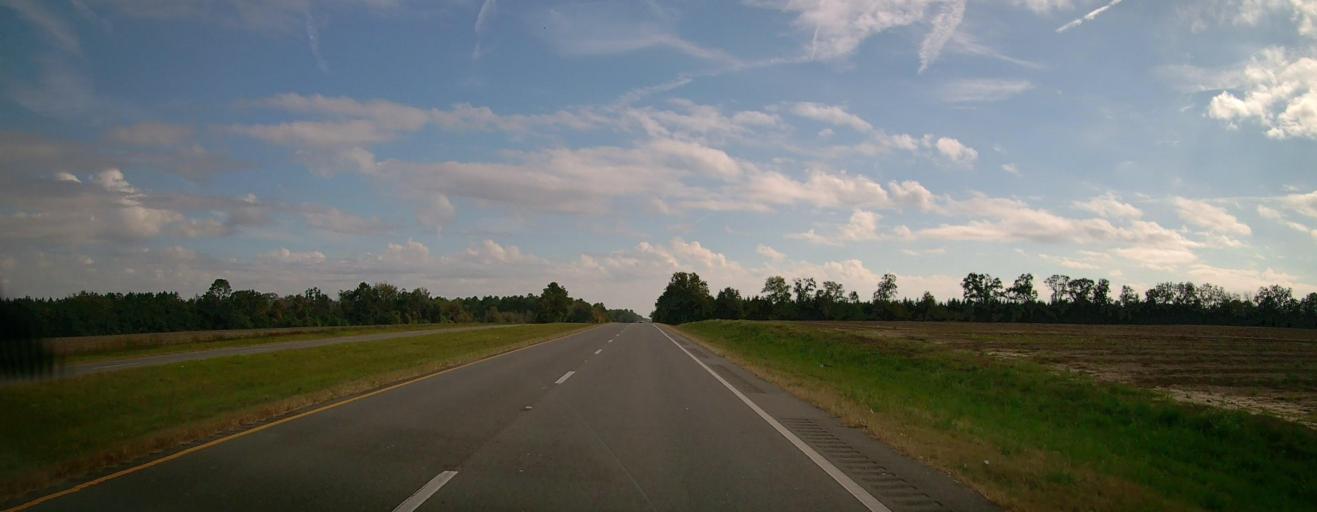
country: US
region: Georgia
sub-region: Thomas County
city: Meigs
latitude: 31.0254
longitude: -84.0600
